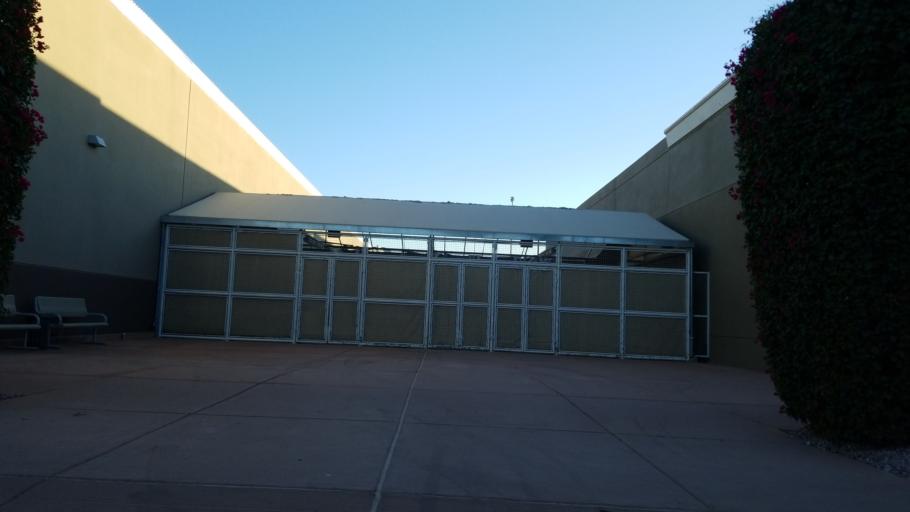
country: US
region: Arizona
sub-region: Maricopa County
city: Paradise Valley
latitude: 33.6749
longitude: -111.9751
